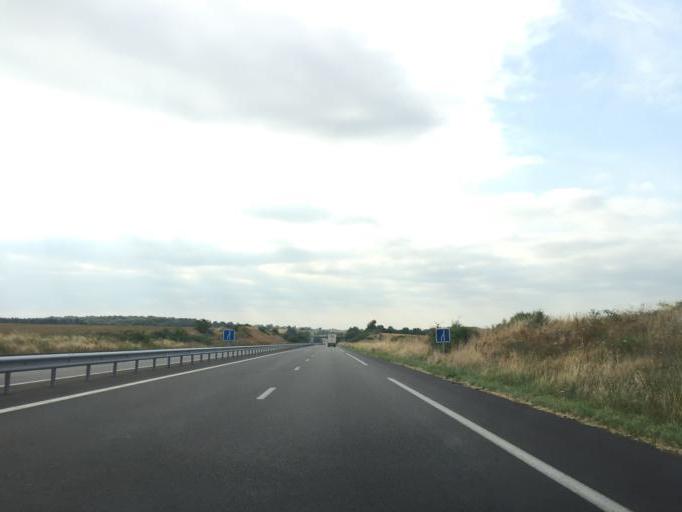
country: FR
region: Auvergne
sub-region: Departement de l'Allier
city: Saint-Francois
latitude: 46.4660
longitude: 3.8825
